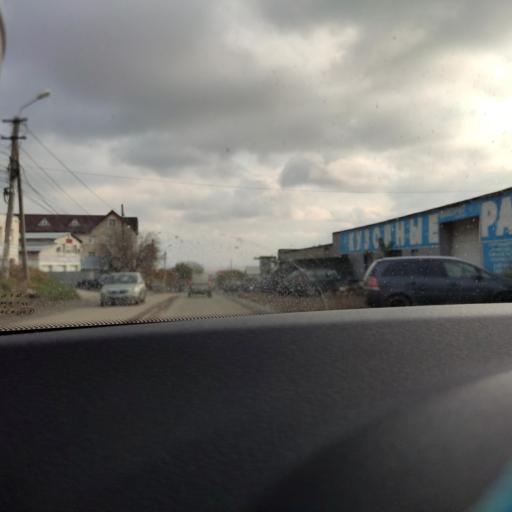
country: RU
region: Samara
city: Samara
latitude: 53.1800
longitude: 50.1667
